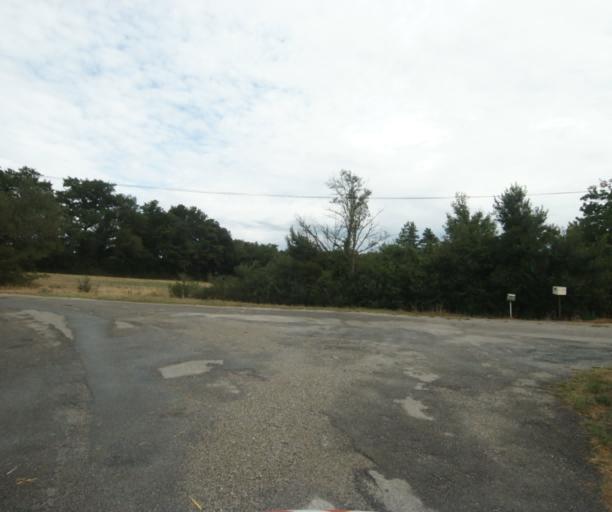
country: FR
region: Midi-Pyrenees
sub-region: Departement de la Haute-Garonne
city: Revel
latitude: 43.4269
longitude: 1.9978
